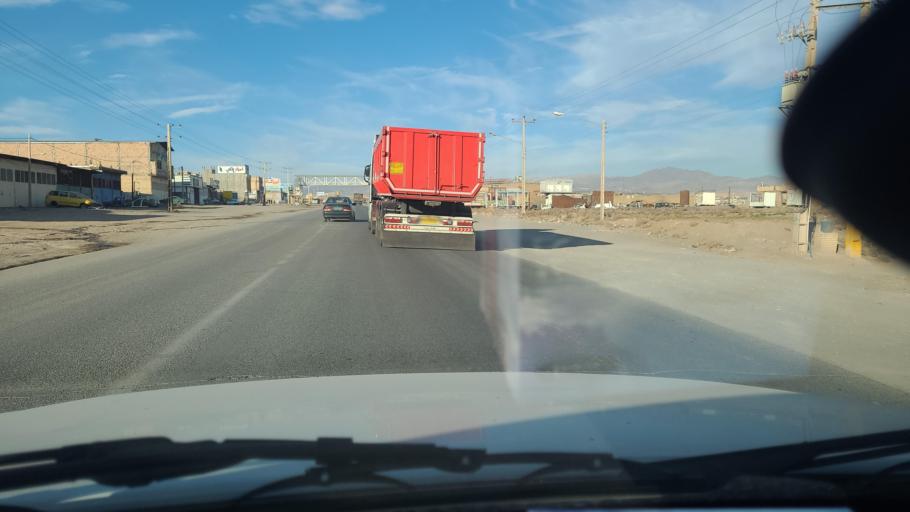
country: IR
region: Razavi Khorasan
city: Sabzevar
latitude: 36.2198
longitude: 57.6514
